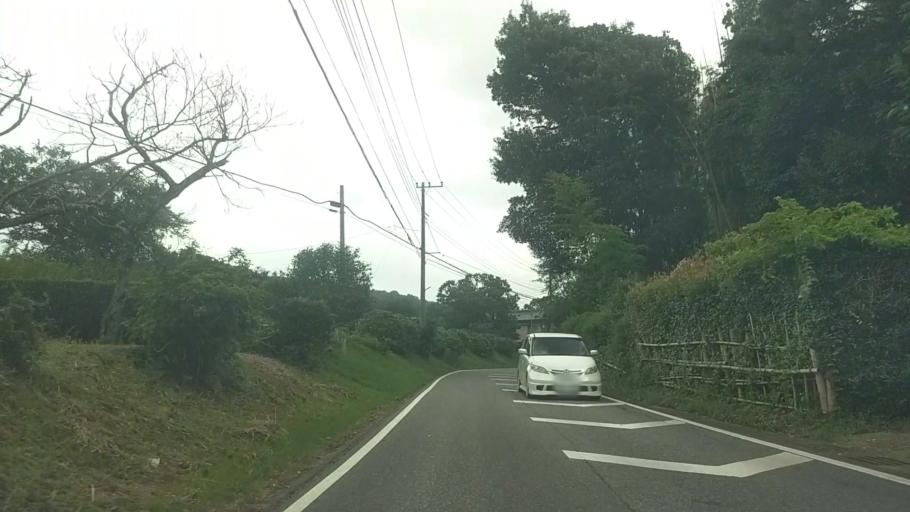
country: JP
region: Chiba
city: Kimitsu
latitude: 35.2294
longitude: 140.0106
